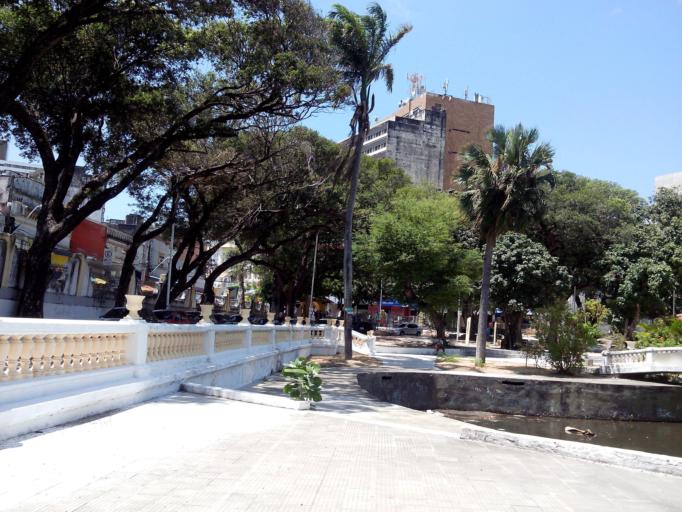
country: BR
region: Ceara
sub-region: Fortaleza
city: Fortaleza
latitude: -3.7314
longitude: -38.5264
